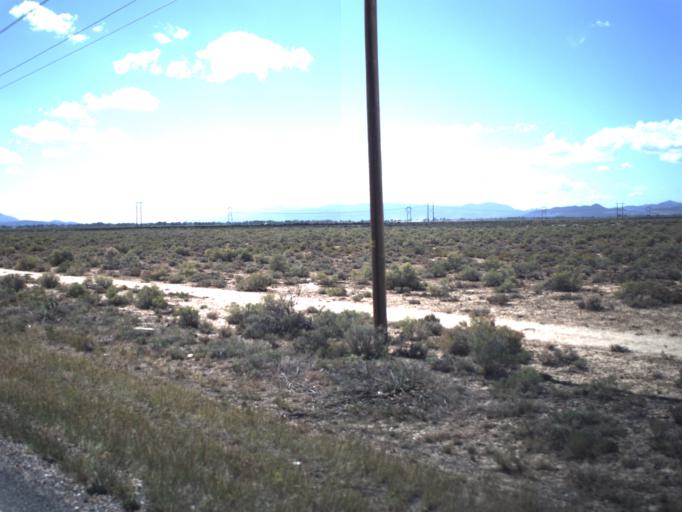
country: US
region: Utah
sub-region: Iron County
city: Enoch
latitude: 37.8091
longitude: -113.0505
